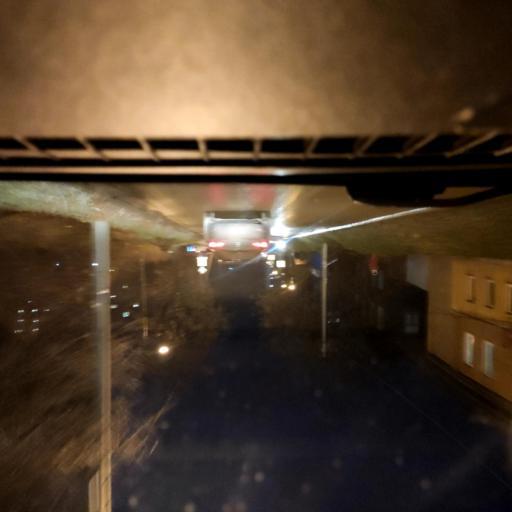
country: RU
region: Perm
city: Perm
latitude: 58.0352
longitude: 56.3209
